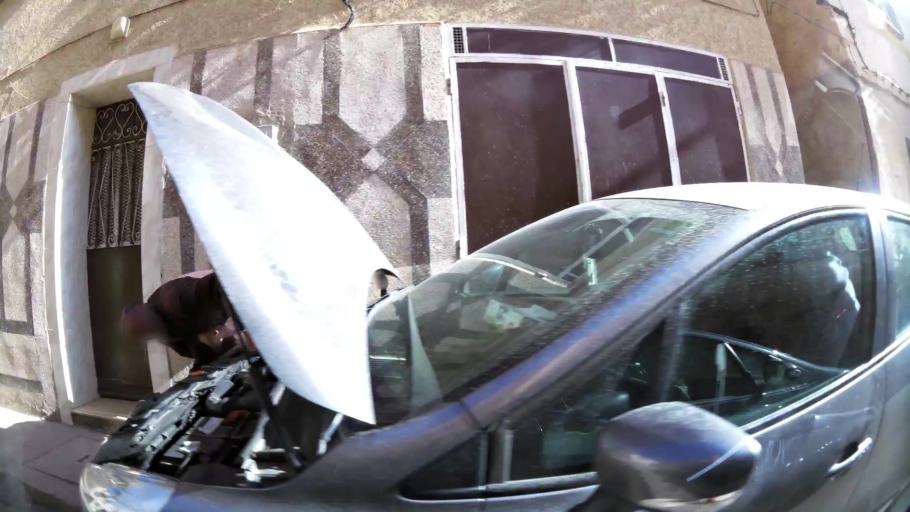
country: MA
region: Oriental
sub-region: Oujda-Angad
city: Oujda
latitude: 34.6762
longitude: -1.9072
